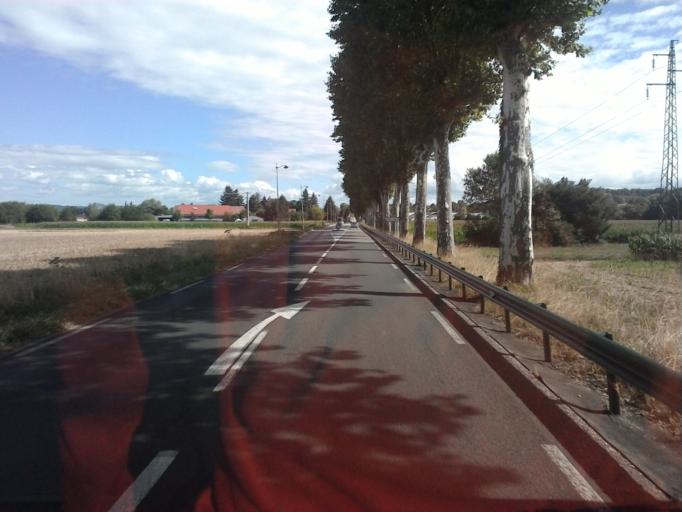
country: FR
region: Rhone-Alpes
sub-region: Departement de l'Ain
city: Ambronay
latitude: 45.9947
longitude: 5.3543
